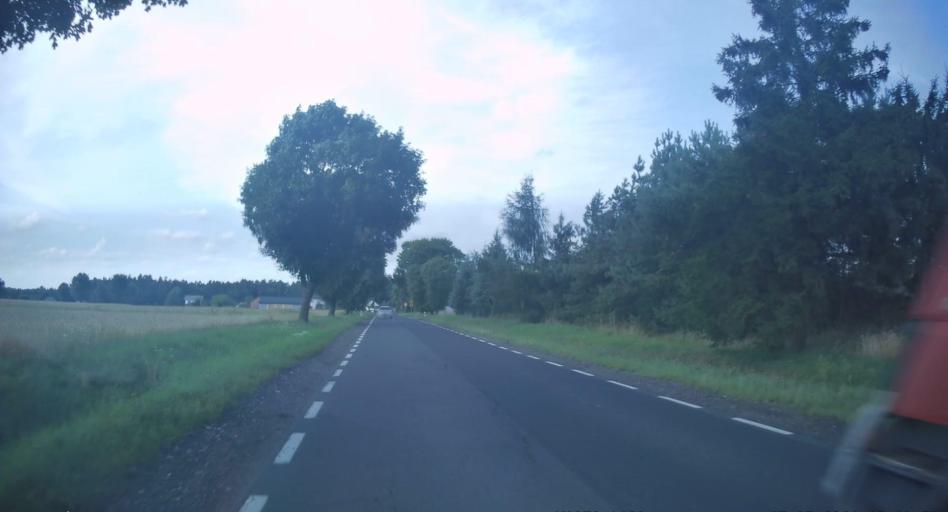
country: PL
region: Lodz Voivodeship
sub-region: Powiat rawski
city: Cieladz
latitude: 51.6798
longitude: 20.2672
